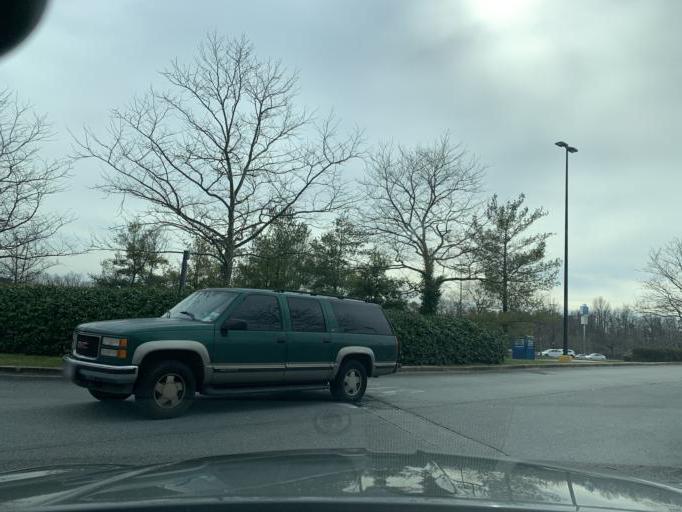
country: US
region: Maryland
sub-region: Anne Arundel County
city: Maryland City
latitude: 39.0996
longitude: -76.8045
